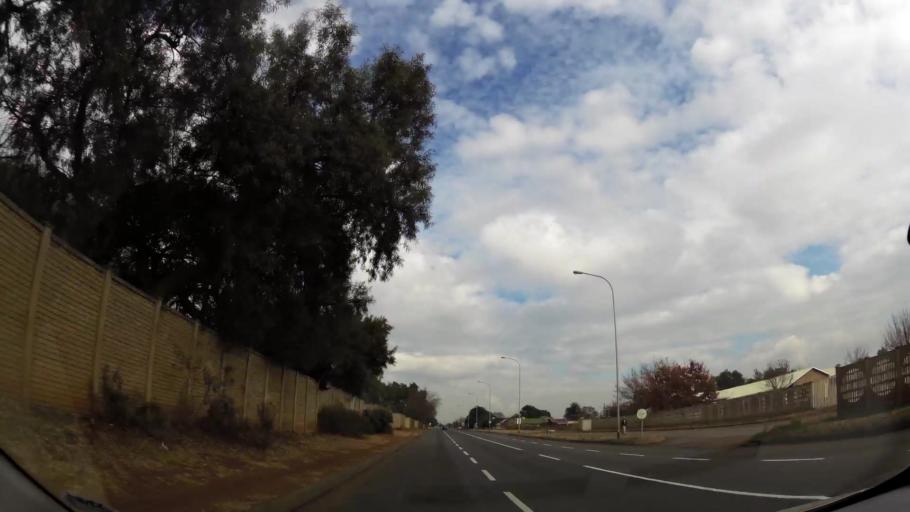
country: ZA
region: Gauteng
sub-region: Sedibeng District Municipality
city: Meyerton
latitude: -26.5923
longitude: 27.9972
